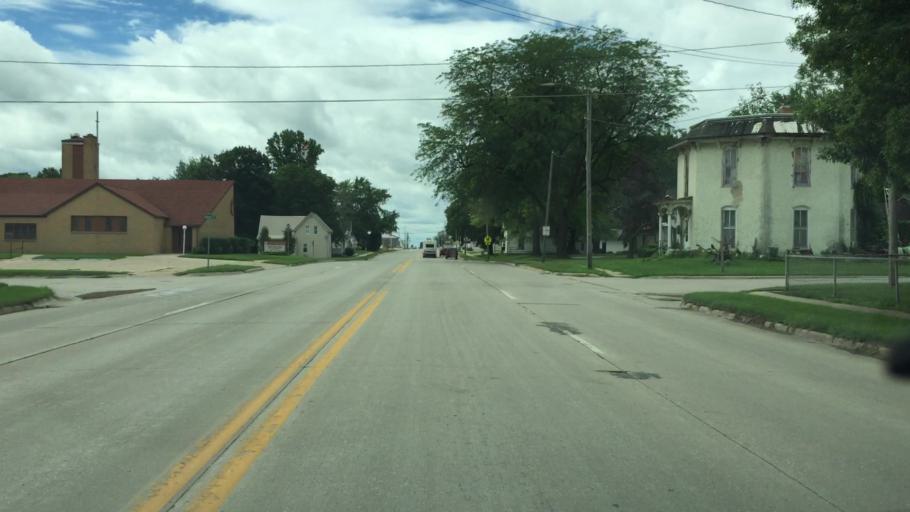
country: US
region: Iowa
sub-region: Jasper County
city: Monroe
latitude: 41.5252
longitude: -93.1018
